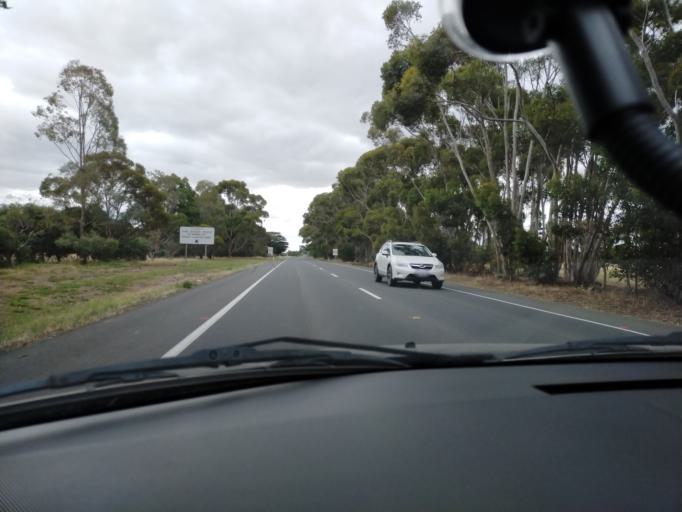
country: AU
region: Victoria
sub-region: Greater Geelong
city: Wandana Heights
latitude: -38.0984
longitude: 144.0743
